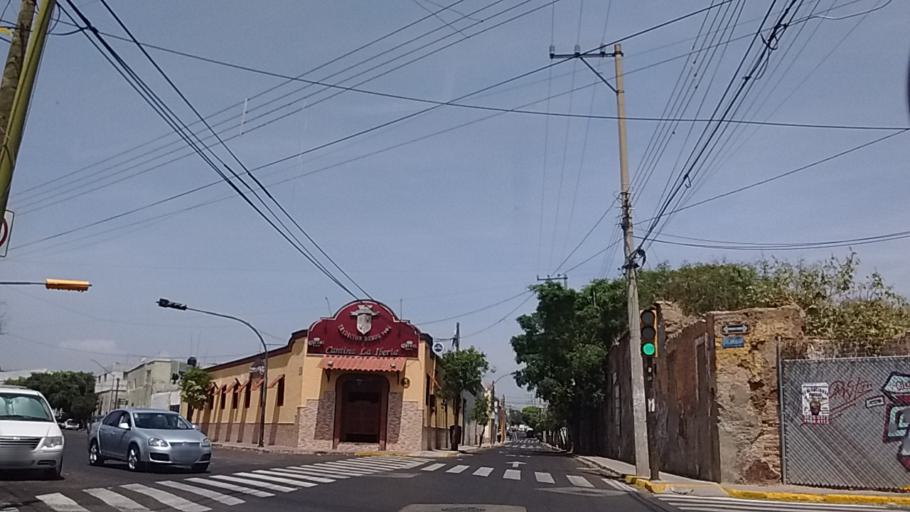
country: MX
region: Jalisco
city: Guadalajara
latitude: 20.6831
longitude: -103.3407
